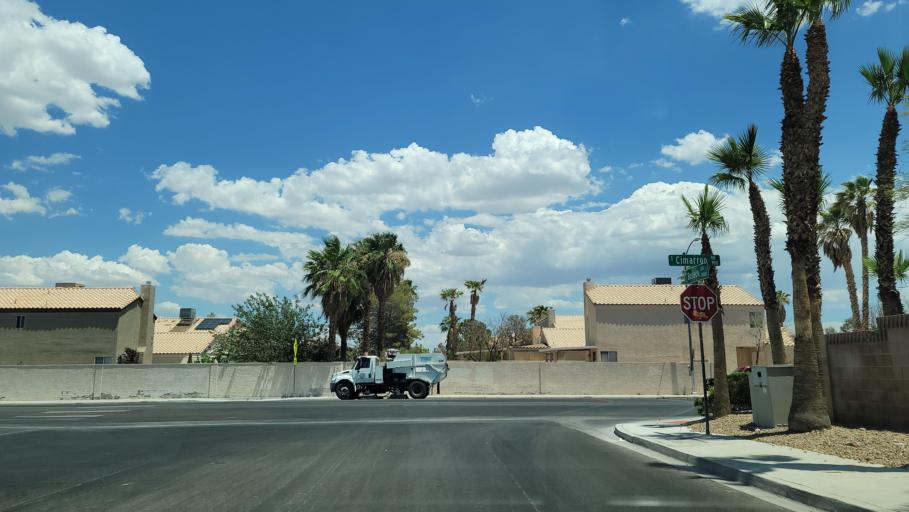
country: US
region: Nevada
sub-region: Clark County
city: Spring Valley
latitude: 36.1628
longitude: -115.2694
